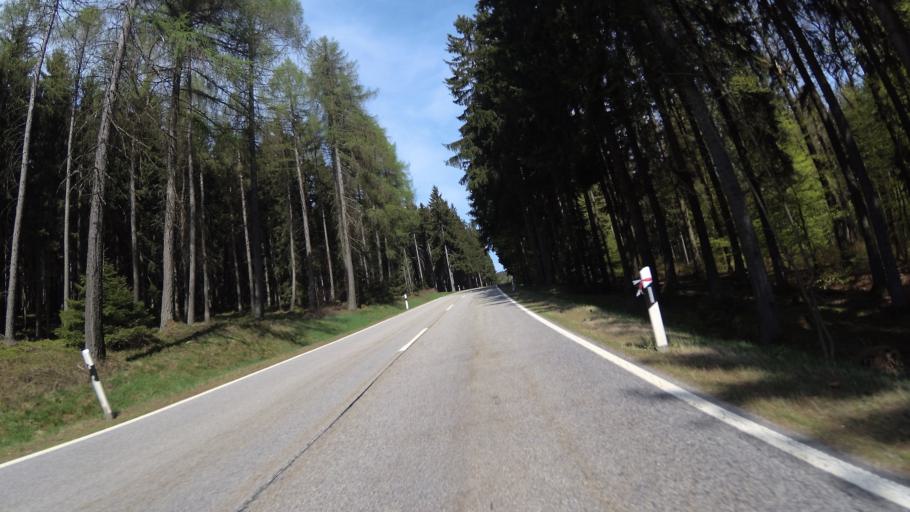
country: DE
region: Rheinland-Pfalz
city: Hattgenstein
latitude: 49.7169
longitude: 7.1358
